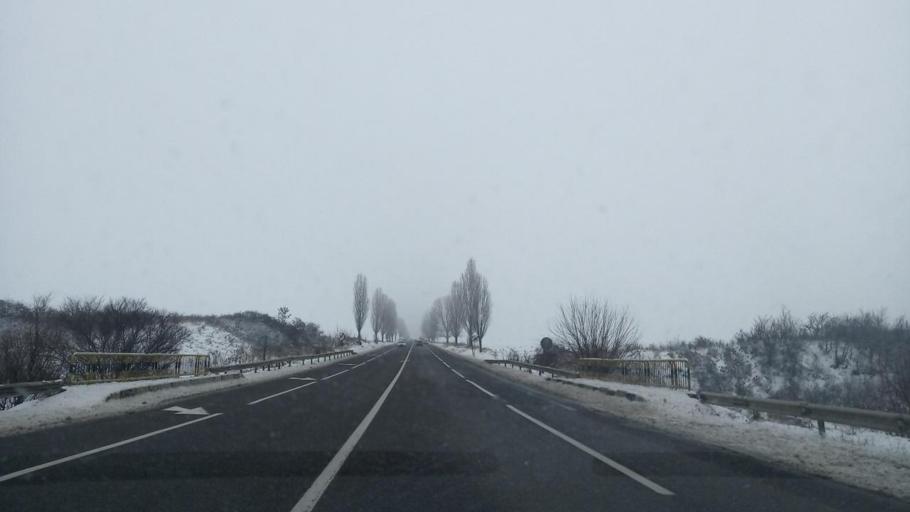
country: RO
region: Bacau
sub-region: Comuna Faraoani
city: Faraoani
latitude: 46.4385
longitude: 26.9213
